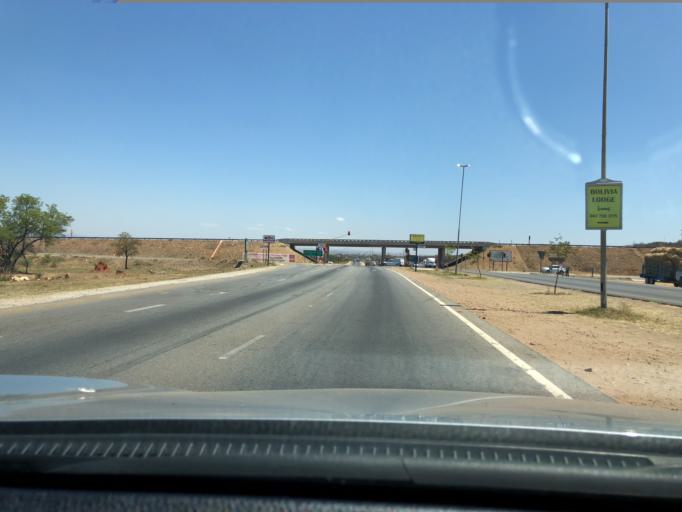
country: ZA
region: Limpopo
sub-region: Capricorn District Municipality
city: Polokwane
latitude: -23.8986
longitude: 29.5115
